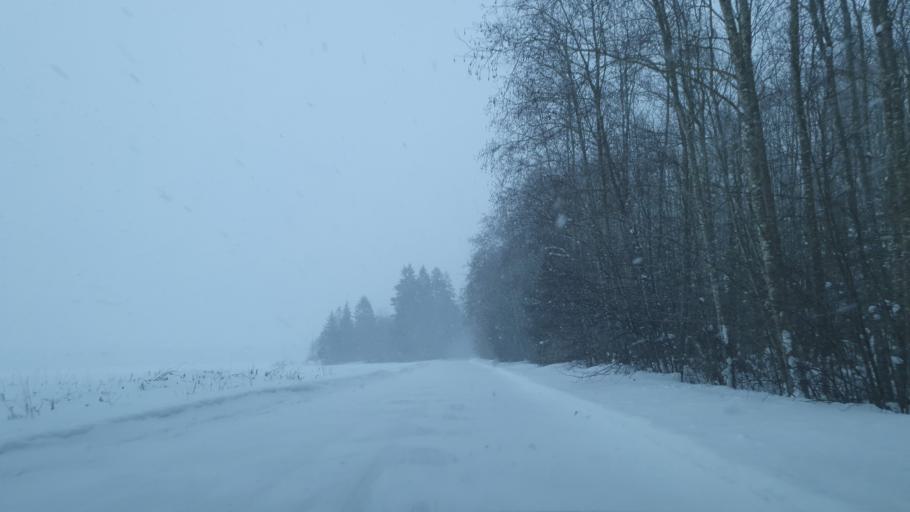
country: EE
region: Jaervamaa
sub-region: Jaerva-Jaani vald
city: Jarva-Jaani
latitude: 59.0657
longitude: 25.8165
